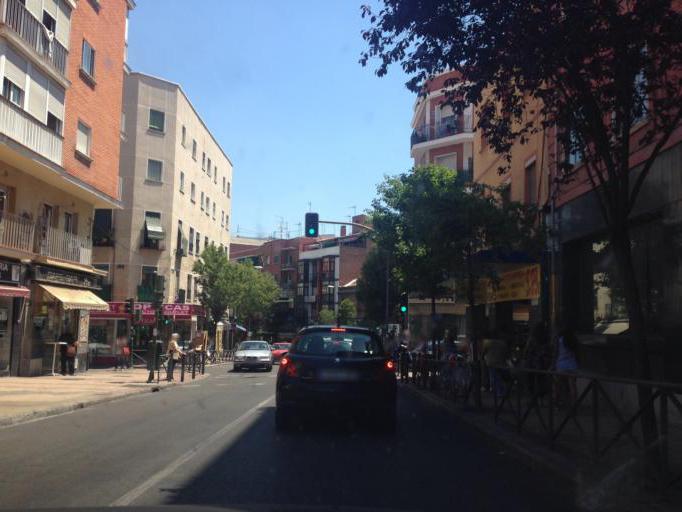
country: ES
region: Madrid
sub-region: Provincia de Madrid
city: Usera
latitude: 40.3862
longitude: -3.7031
